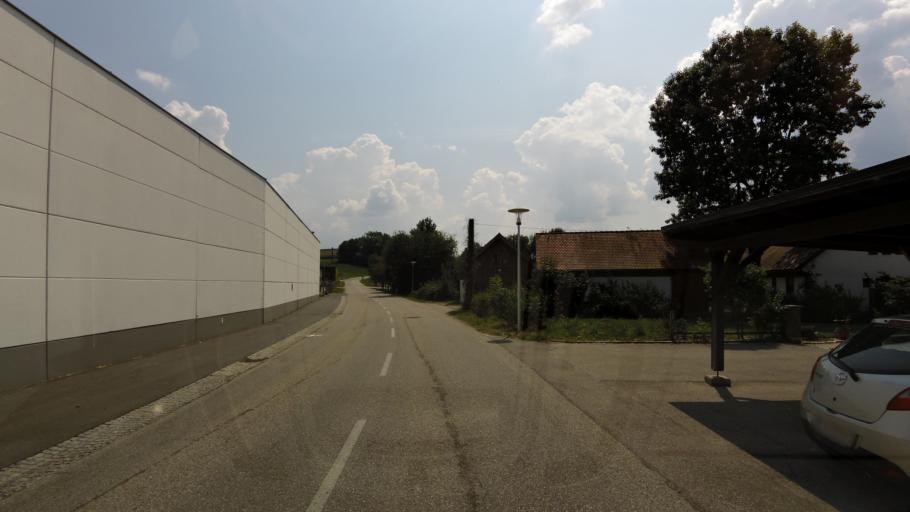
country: AT
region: Upper Austria
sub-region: Politischer Bezirk Ried im Innkreis
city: Waldzell
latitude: 48.1653
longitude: 13.4205
